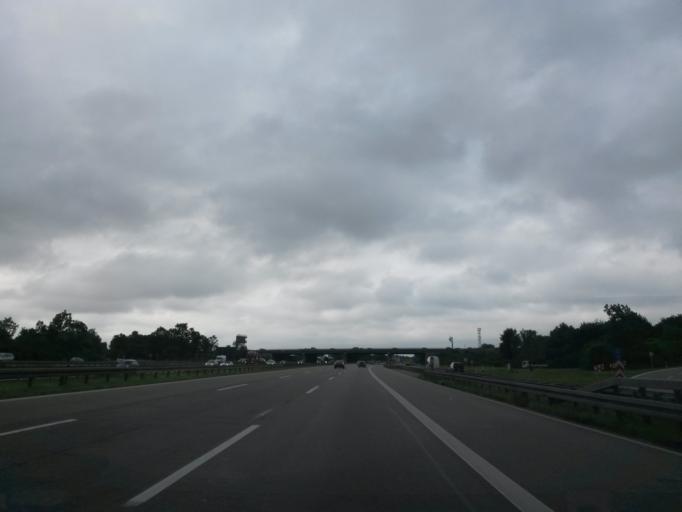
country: DE
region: Bavaria
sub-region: Upper Bavaria
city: Feldkirchen
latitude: 48.1458
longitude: 11.7566
